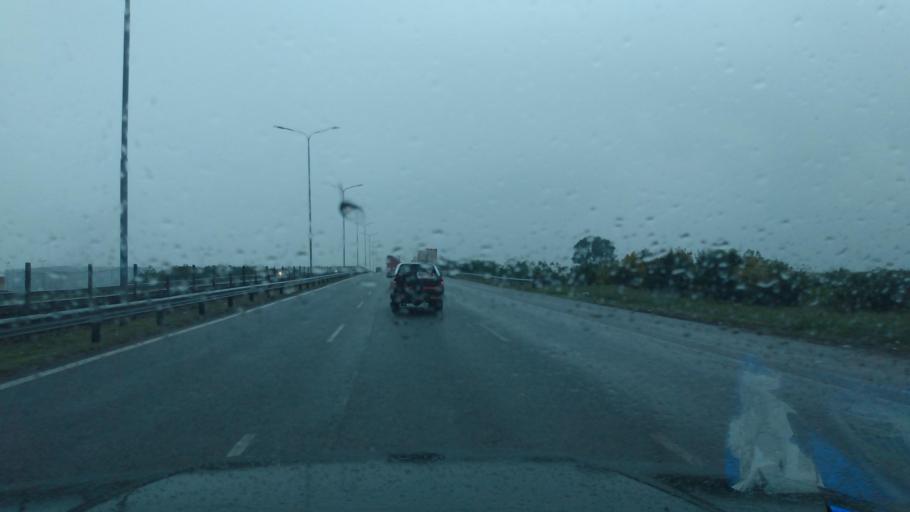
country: AR
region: Buenos Aires
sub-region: Partido de Tigre
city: Tigre
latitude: -34.5068
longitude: -58.5900
